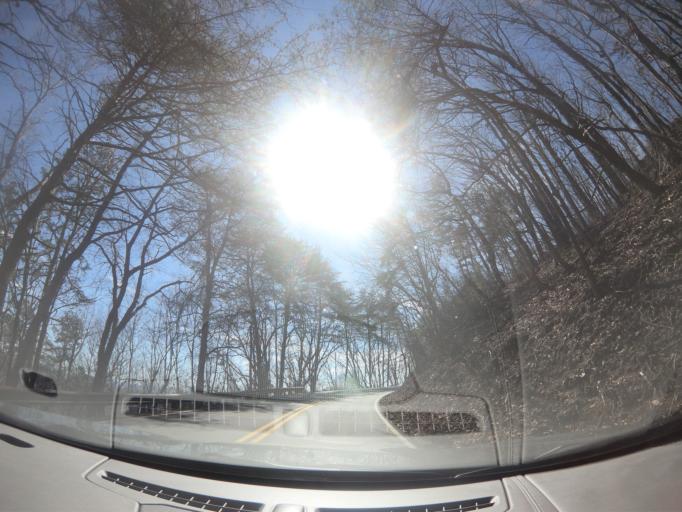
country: US
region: Tennessee
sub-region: Hamilton County
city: Lookout Mountain
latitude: 34.9823
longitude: -85.3450
